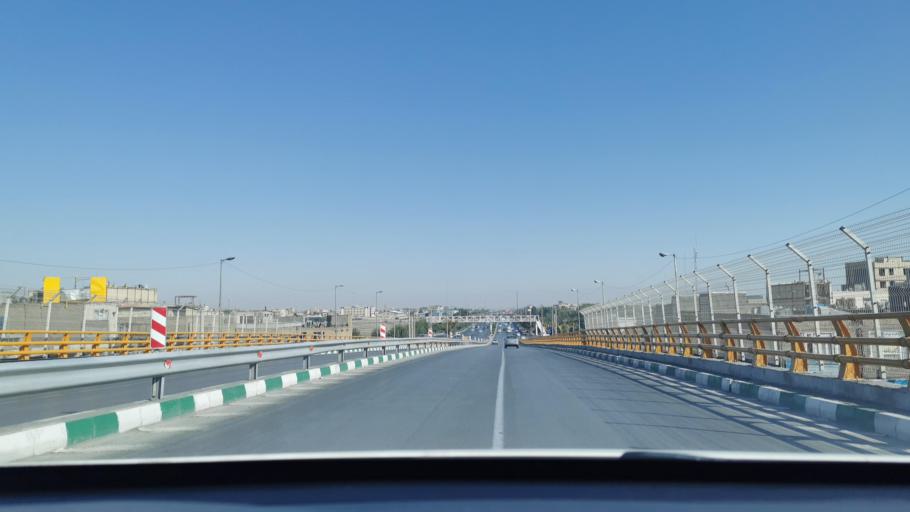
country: IR
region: Razavi Khorasan
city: Mashhad
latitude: 36.3288
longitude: 59.6243
